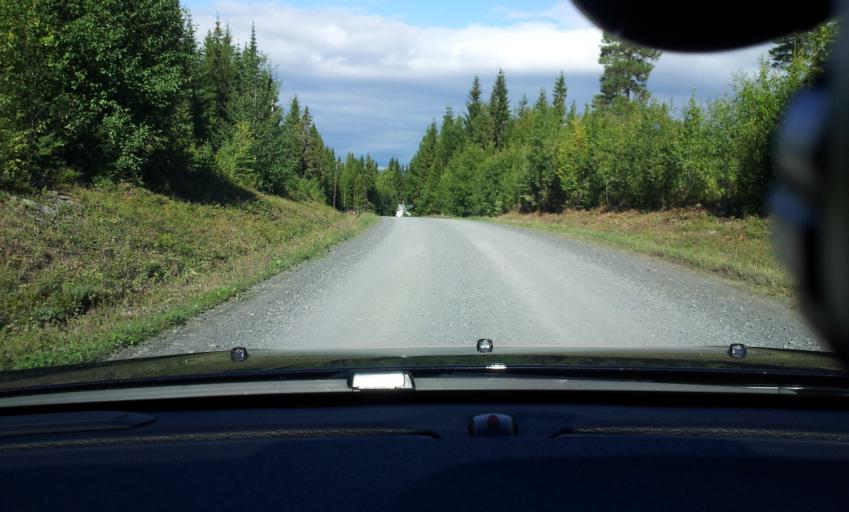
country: SE
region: Jaemtland
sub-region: Are Kommun
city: Jarpen
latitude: 63.2799
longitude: 13.7319
